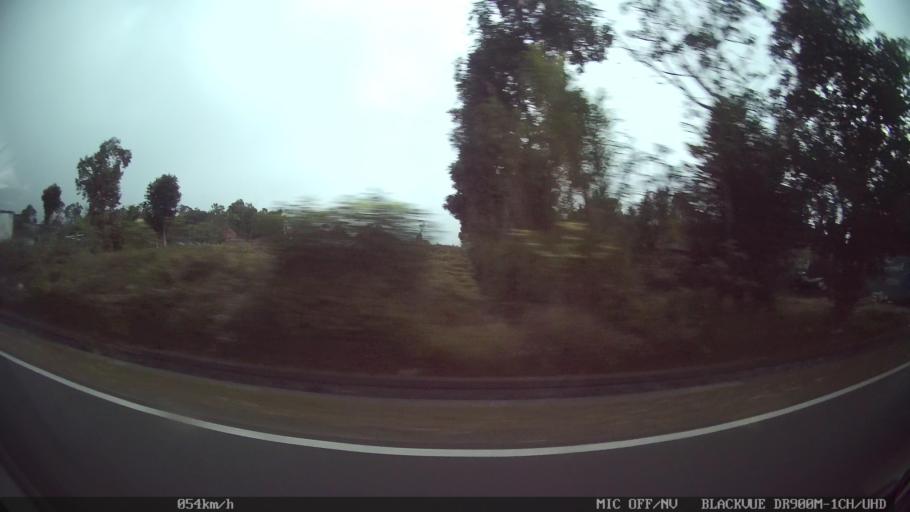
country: ID
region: Bali
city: Banjar Kedisan
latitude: -8.2866
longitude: 115.3195
